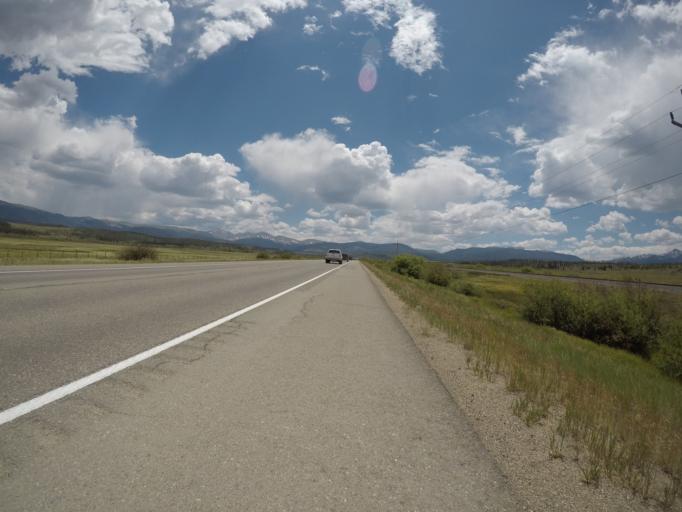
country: US
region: Colorado
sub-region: Grand County
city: Fraser
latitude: 39.9696
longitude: -105.8247
